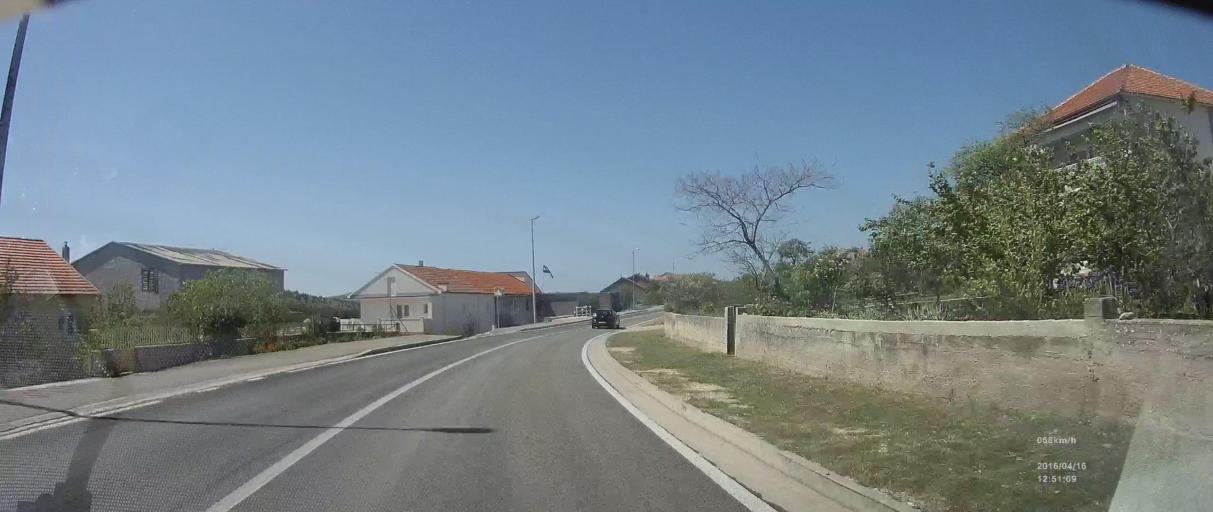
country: HR
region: Sibensko-Kniniska
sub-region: Grad Sibenik
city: Brodarica
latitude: 43.6743
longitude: 16.0059
